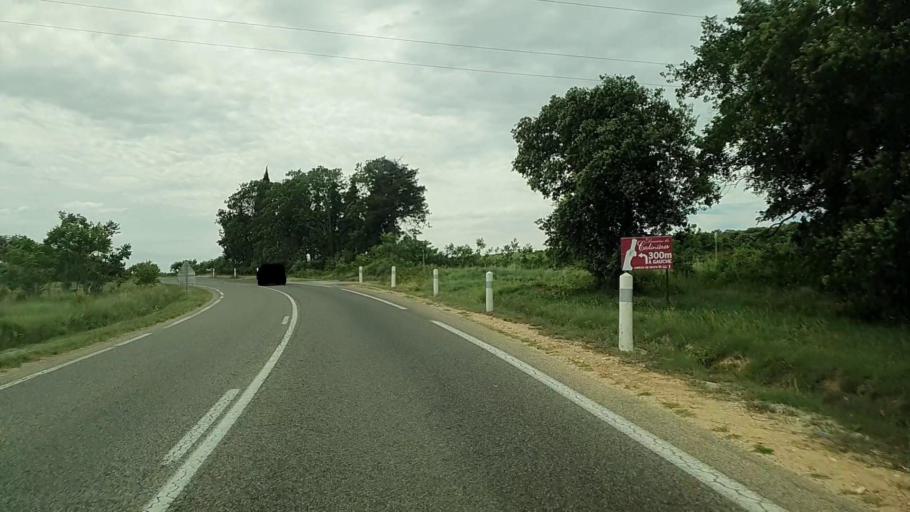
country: FR
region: Languedoc-Roussillon
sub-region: Departement du Gard
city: Connaux
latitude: 44.0592
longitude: 4.5704
